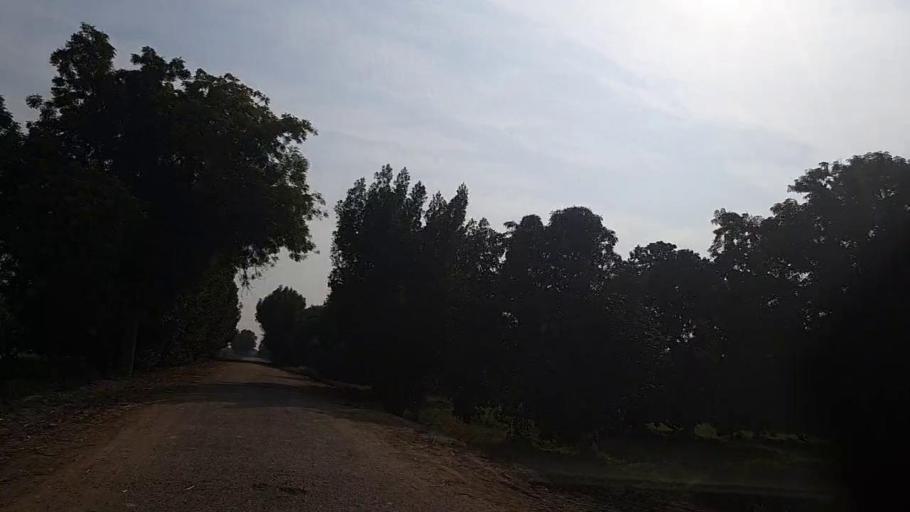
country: PK
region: Sindh
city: Daur
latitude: 26.4016
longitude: 68.2133
